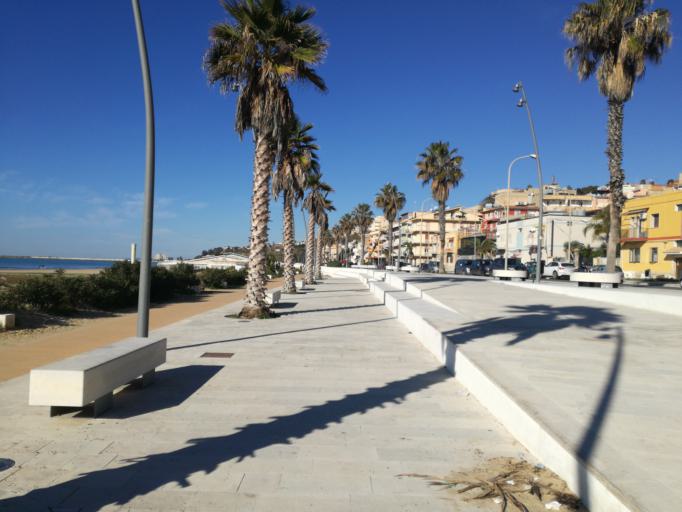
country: IT
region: Sicily
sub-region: Provincia di Caltanissetta
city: Gela
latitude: 37.0647
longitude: 14.2465
